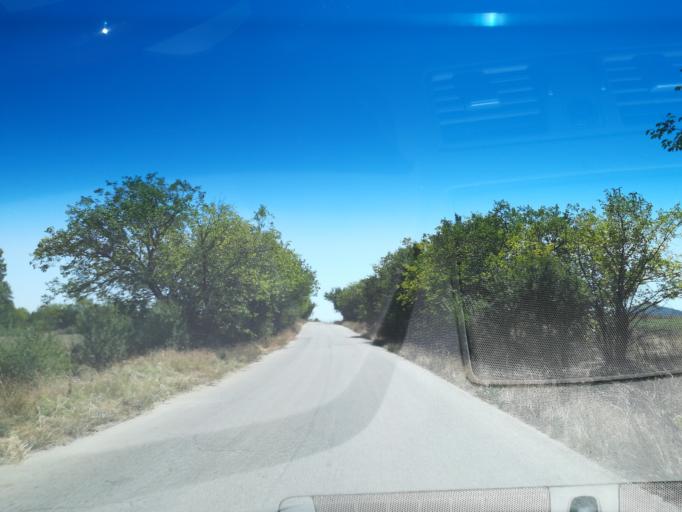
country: BG
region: Pazardzhik
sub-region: Obshtina Strelcha
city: Strelcha
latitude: 42.3573
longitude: 24.3991
